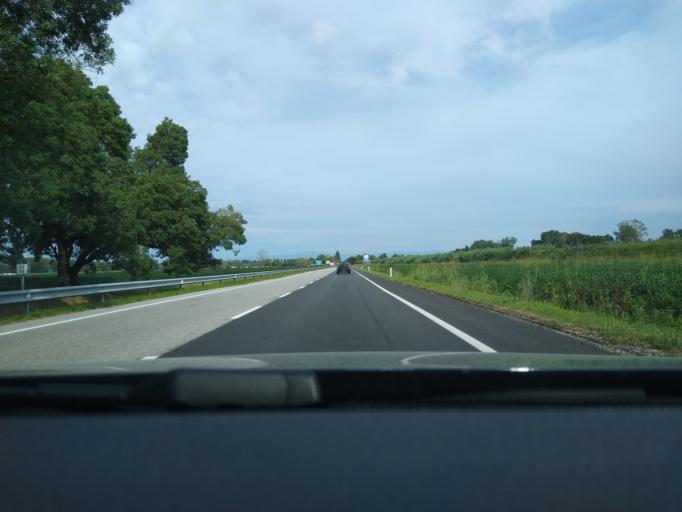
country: IT
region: Veneto
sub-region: Provincia di Venezia
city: Bibione
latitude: 45.6764
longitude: 13.0510
